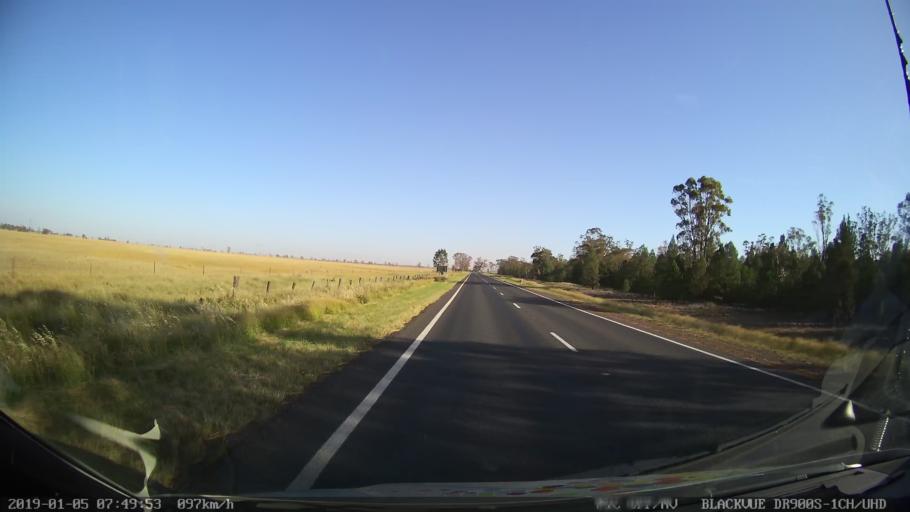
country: AU
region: New South Wales
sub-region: Gilgandra
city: Gilgandra
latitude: -31.7951
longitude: 148.6358
